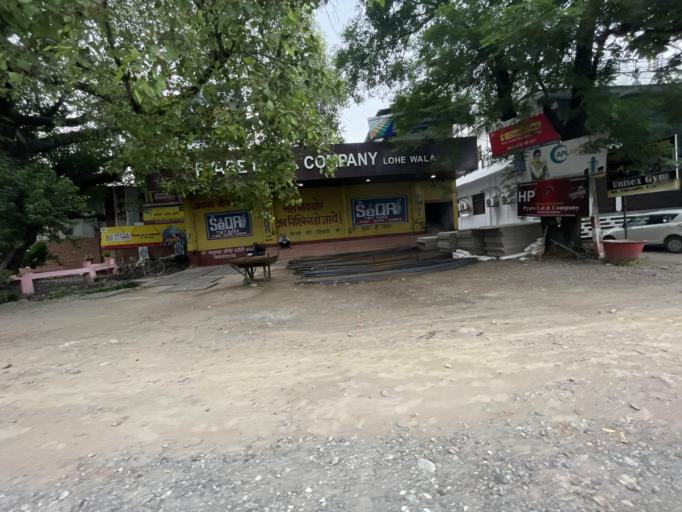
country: IN
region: Uttarakhand
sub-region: Naini Tal
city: Haldwani
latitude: 29.1977
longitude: 79.5127
